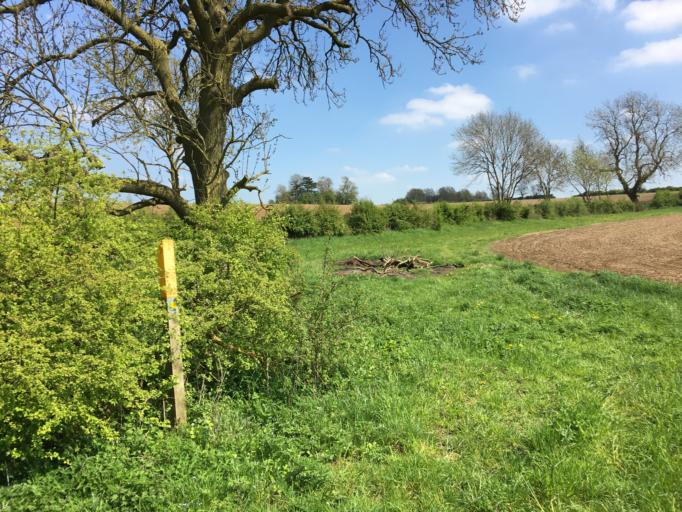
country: GB
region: England
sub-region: Leicestershire
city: Houghton on the Hill
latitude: 52.6113
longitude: -0.9874
